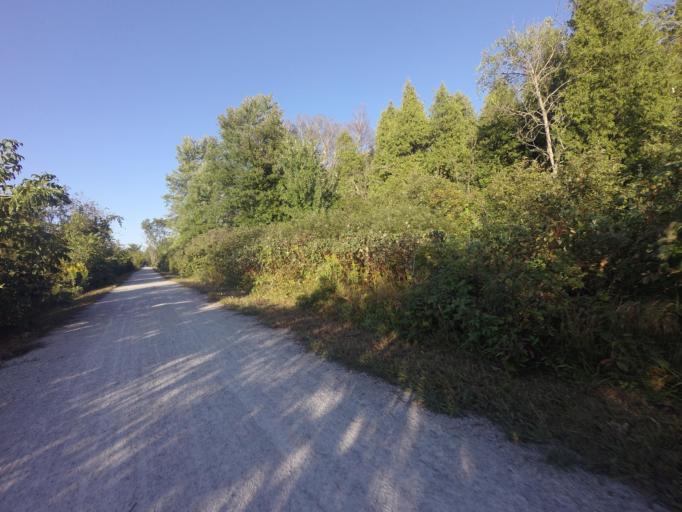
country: CA
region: Ontario
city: Orangeville
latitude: 43.8179
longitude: -79.9250
